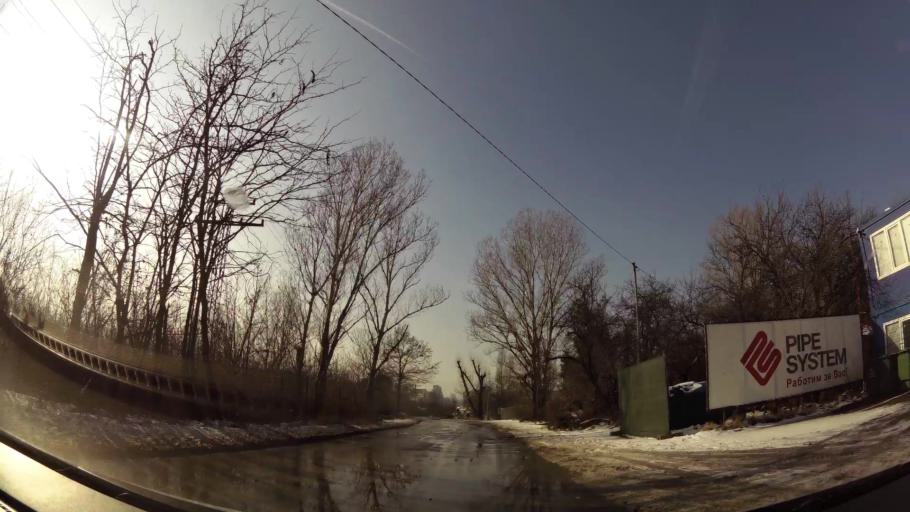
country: BG
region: Sofia-Capital
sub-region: Stolichna Obshtina
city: Sofia
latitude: 42.6568
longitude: 23.3254
